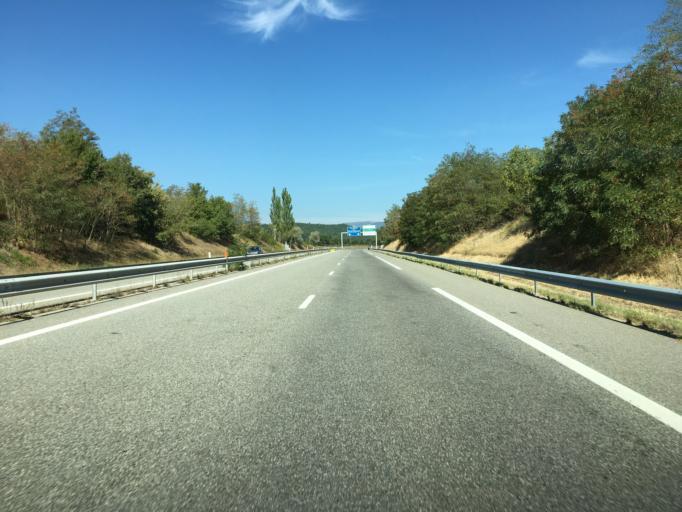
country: FR
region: Provence-Alpes-Cote d'Azur
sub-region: Departement des Alpes-de-Haute-Provence
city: Sisteron
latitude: 44.2158
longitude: 5.9251
